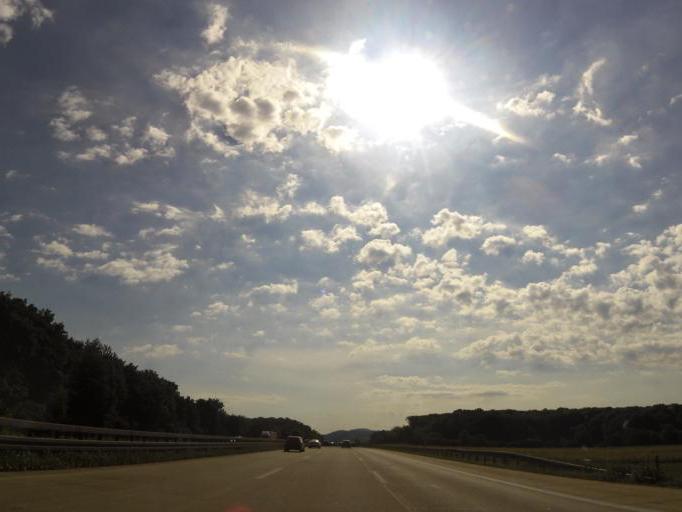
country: DE
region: Baden-Wuerttemberg
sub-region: Regierungsbezirk Stuttgart
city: Holzmaden
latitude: 48.6292
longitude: 9.4905
